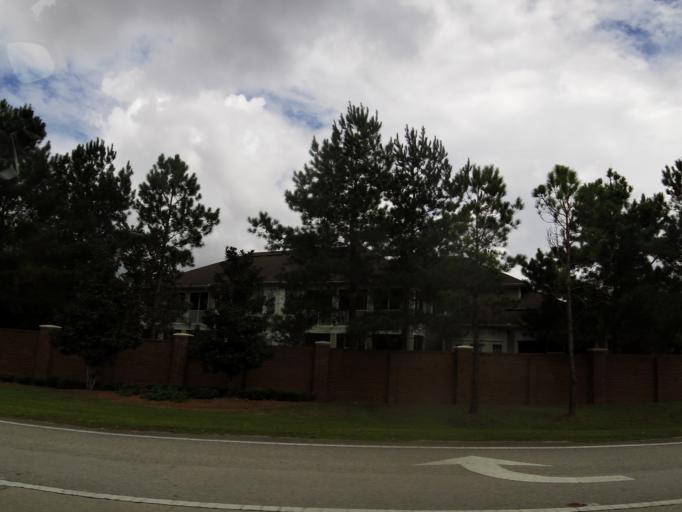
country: US
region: Florida
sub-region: Clay County
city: Lakeside
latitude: 30.1023
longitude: -81.7257
